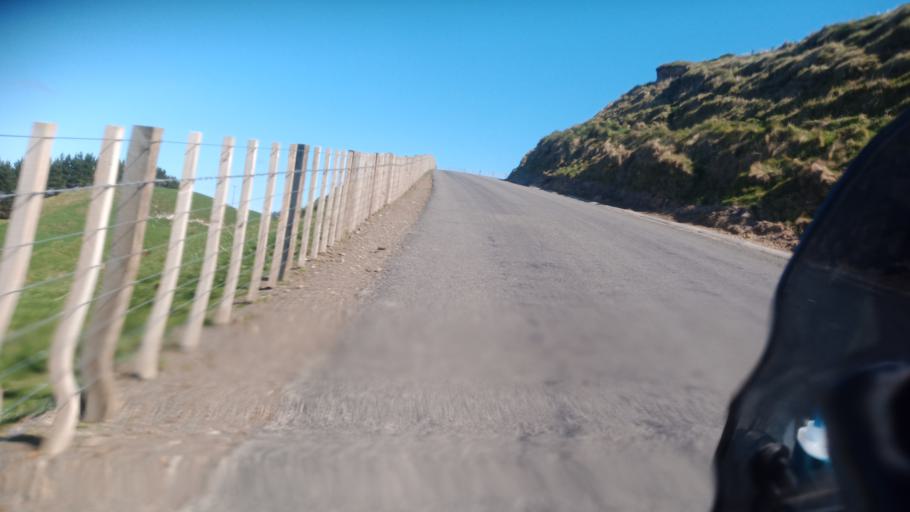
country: NZ
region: Gisborne
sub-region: Gisborne District
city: Gisborne
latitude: -39.1602
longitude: 177.9052
